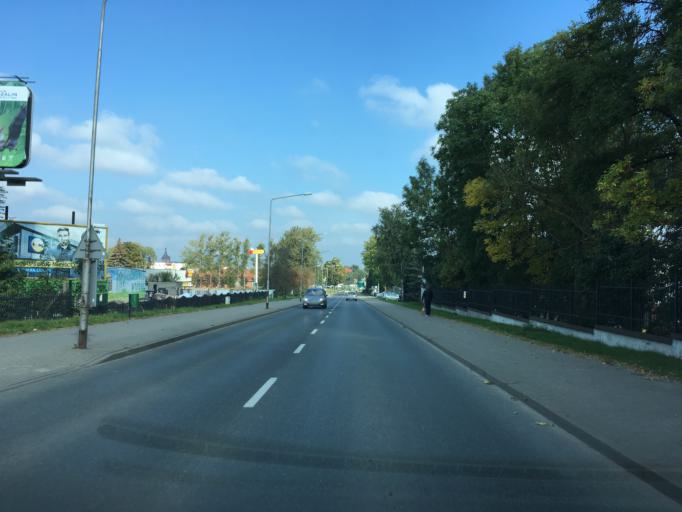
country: PL
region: West Pomeranian Voivodeship
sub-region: Koszalin
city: Koszalin
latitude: 54.1801
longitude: 16.1851
